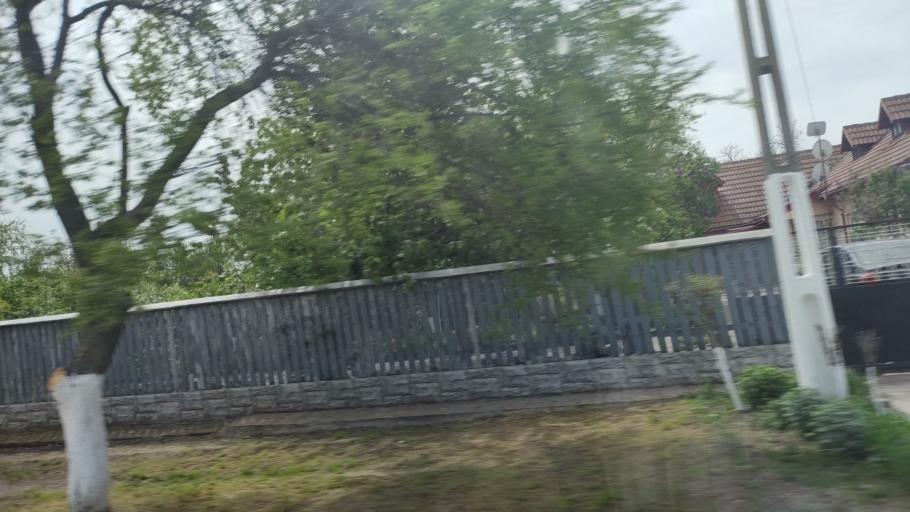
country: RO
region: Constanta
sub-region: Comuna Cobadin
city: Viisoara
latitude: 44.0770
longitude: 28.1892
